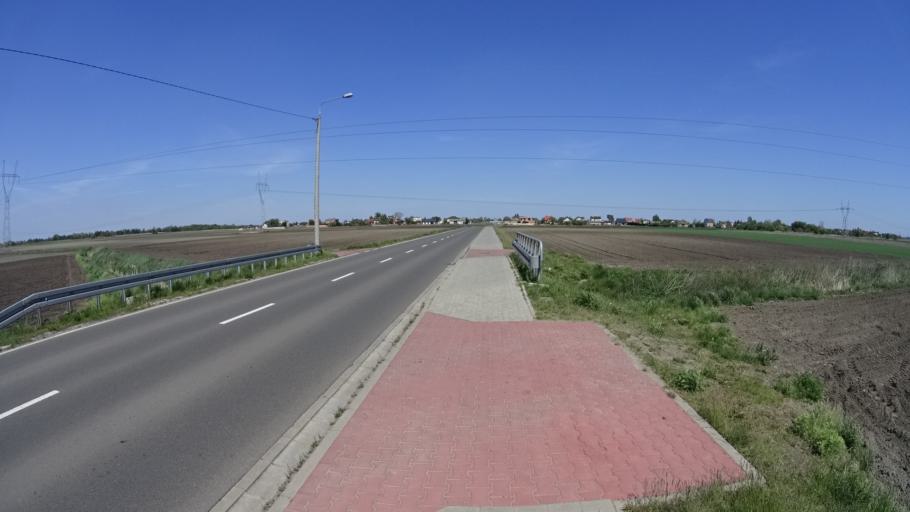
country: PL
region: Masovian Voivodeship
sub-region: Powiat warszawski zachodni
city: Jozefow
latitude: 52.2358
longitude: 20.7377
